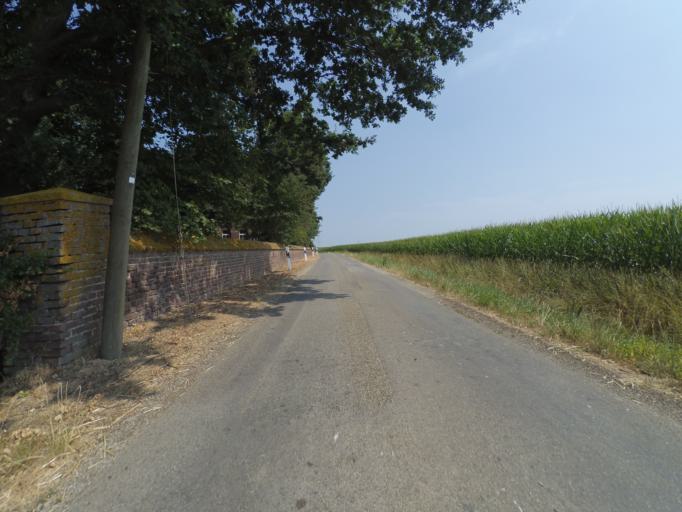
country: DE
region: North Rhine-Westphalia
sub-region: Regierungsbezirk Dusseldorf
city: Mehrhoog
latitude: 51.7371
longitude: 6.4656
